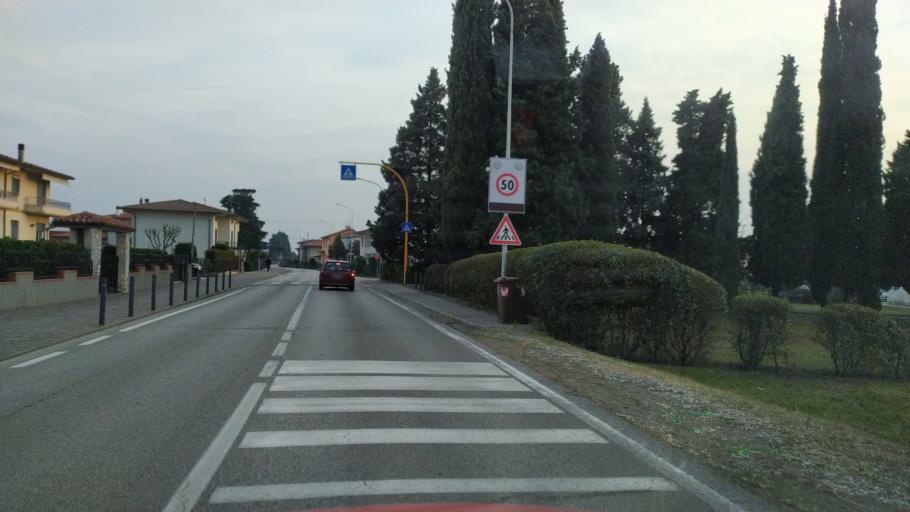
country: IT
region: Veneto
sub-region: Provincia di Vicenza
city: Sarcedo
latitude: 45.6985
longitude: 11.5313
